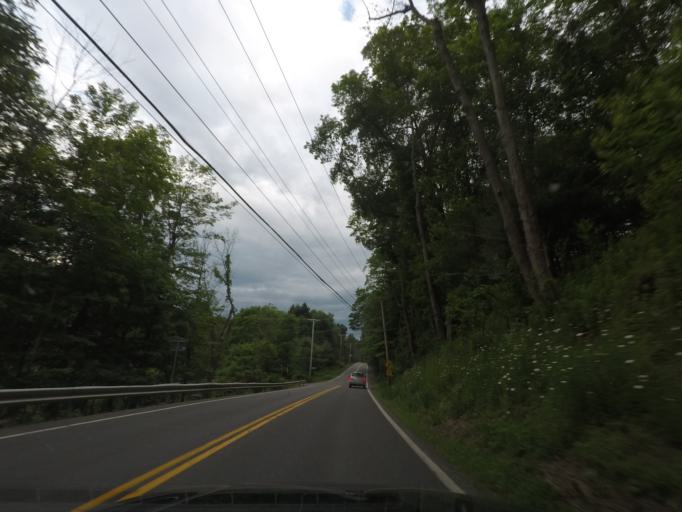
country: US
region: New York
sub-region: Dutchess County
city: Pine Plains
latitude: 41.9650
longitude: -73.7359
